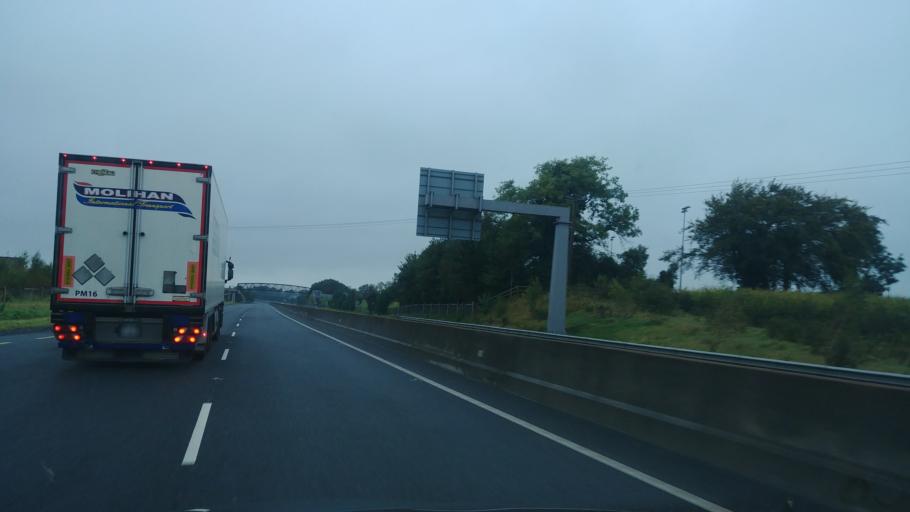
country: IE
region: Leinster
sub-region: An Iarmhi
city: Rochfortbridge
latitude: 53.5040
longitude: -7.2407
